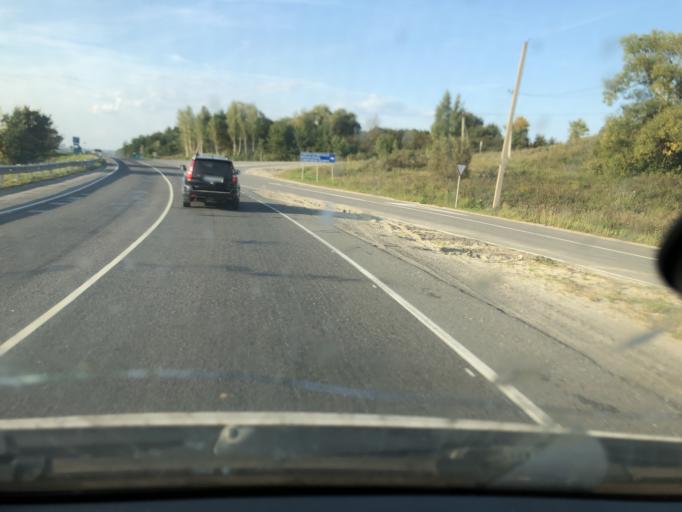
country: RU
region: Kaluga
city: Peremyshl'
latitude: 54.2963
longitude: 36.1794
